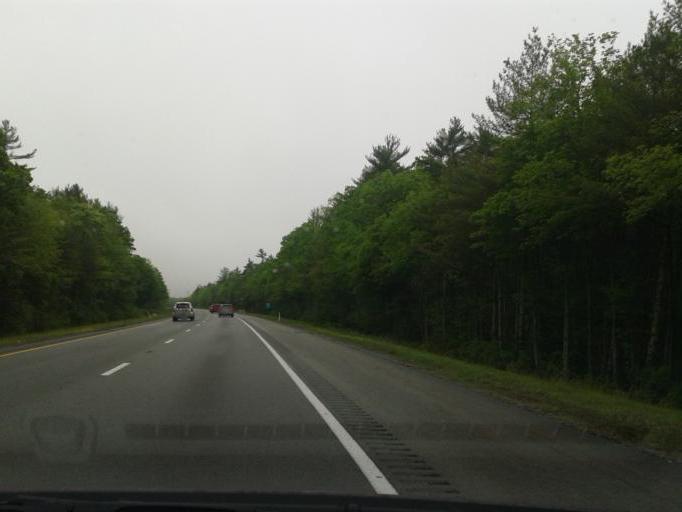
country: US
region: Massachusetts
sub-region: Plymouth County
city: Rochester
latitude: 41.7037
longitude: -70.7990
